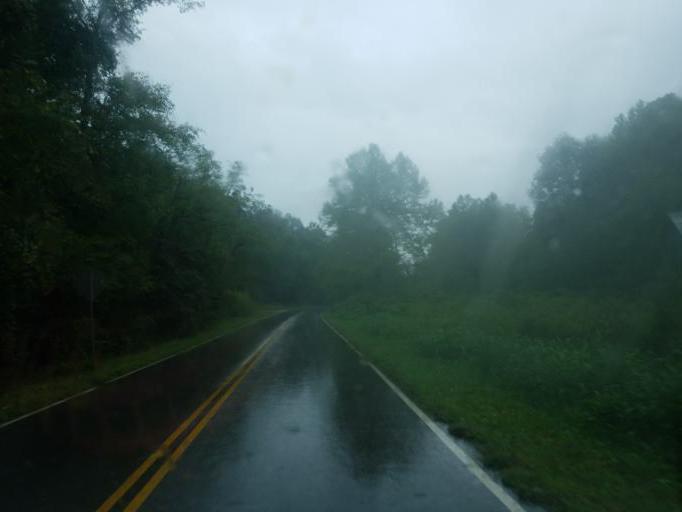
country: US
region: Kentucky
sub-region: Carter County
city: Grayson
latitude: 38.4929
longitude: -82.9925
